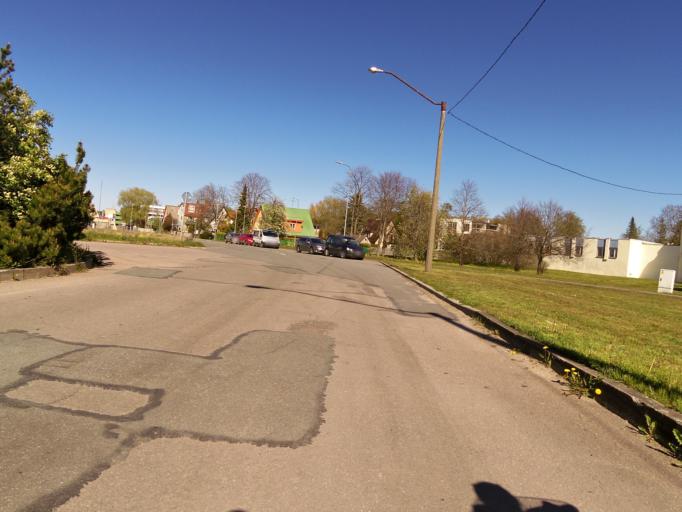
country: EE
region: Harju
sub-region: Viimsi vald
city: Viimsi
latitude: 59.4630
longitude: 24.8211
